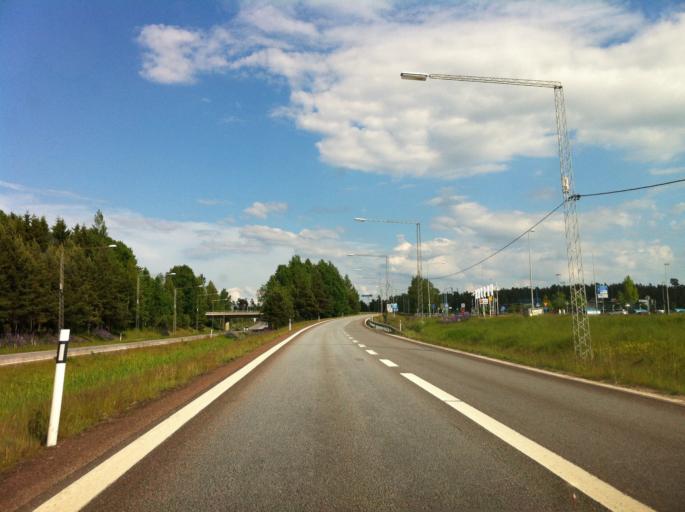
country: SE
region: Vaermland
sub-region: Hammaro Kommun
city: Skoghall
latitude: 59.3811
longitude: 13.4211
